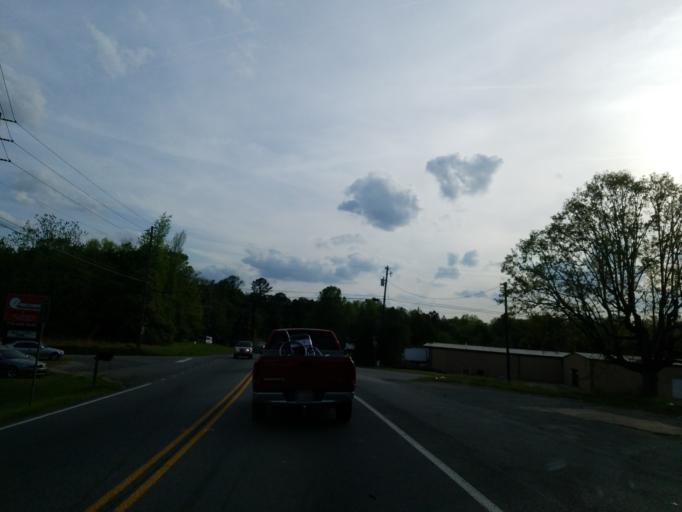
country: US
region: Georgia
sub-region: Cherokee County
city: Canton
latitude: 34.2396
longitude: -84.4294
